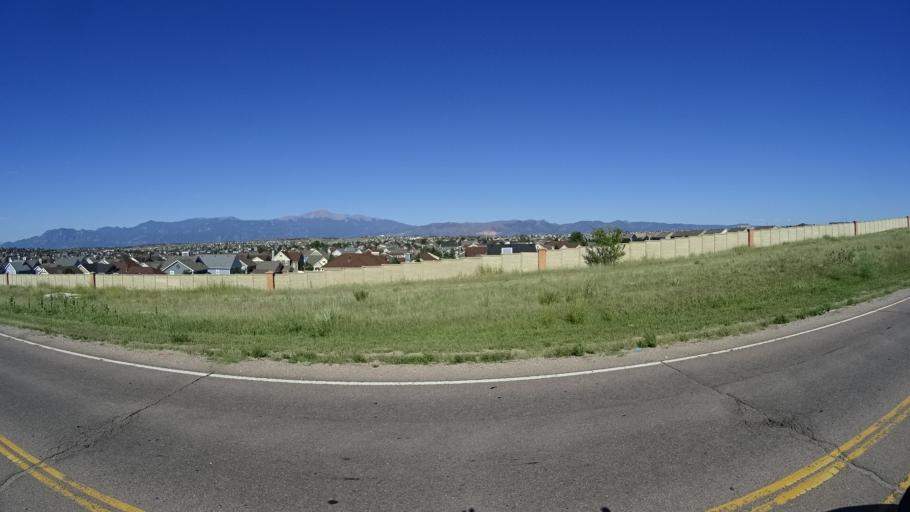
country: US
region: Colorado
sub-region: El Paso County
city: Cimarron Hills
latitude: 38.9151
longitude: -104.6830
